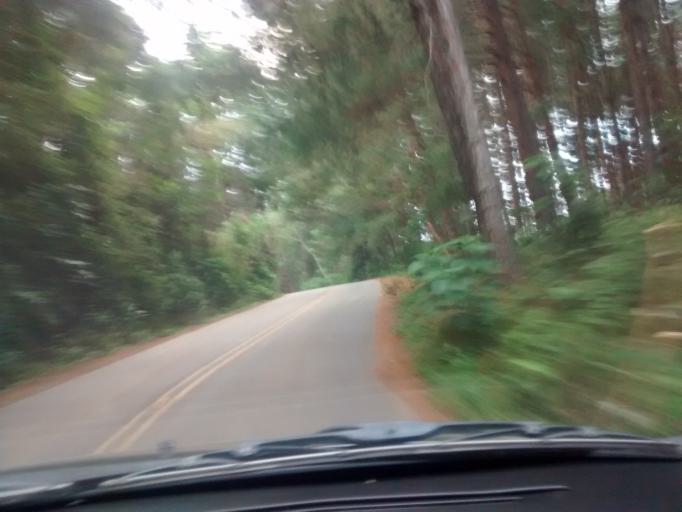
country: BR
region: Sao Paulo
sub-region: Campos Do Jordao
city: Campos do Jordao
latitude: -22.6475
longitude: -45.6312
